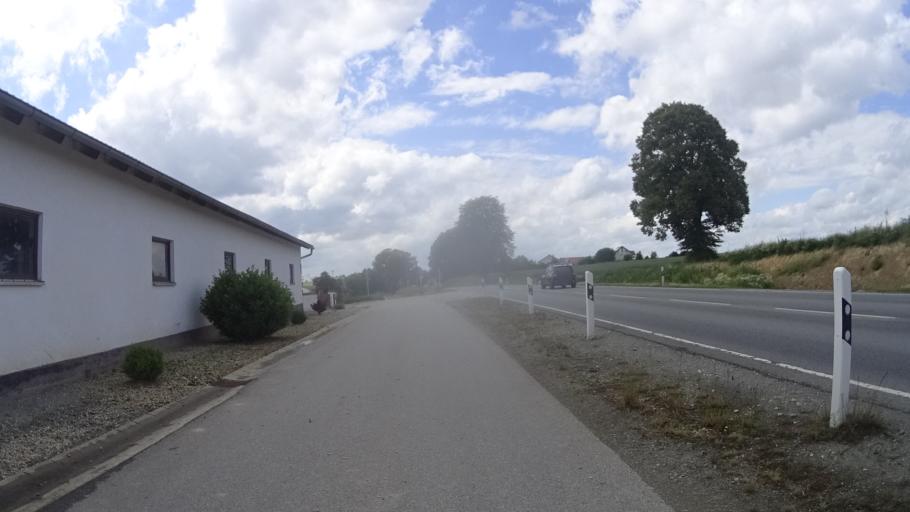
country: DE
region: Bavaria
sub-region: Lower Bavaria
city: Massing
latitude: 48.3952
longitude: 12.6390
